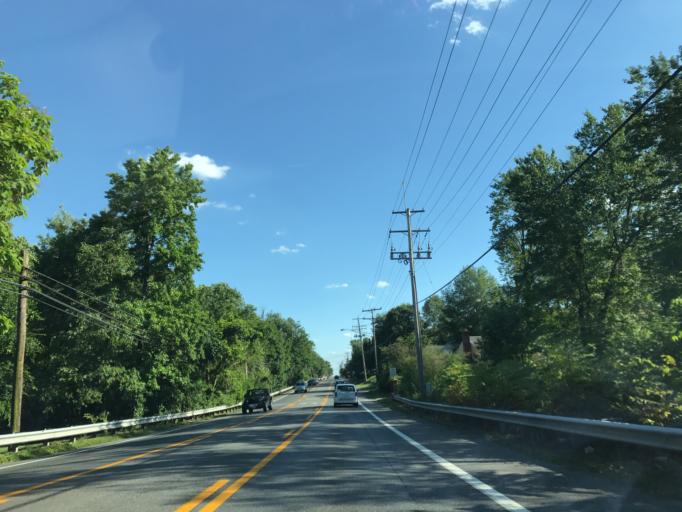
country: US
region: Maryland
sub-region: Anne Arundel County
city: Severn
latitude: 39.1149
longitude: -76.6915
